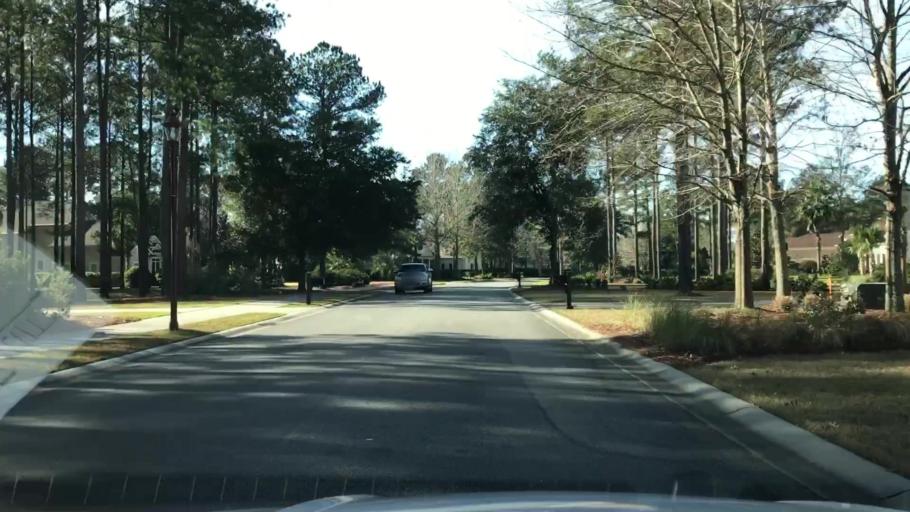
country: US
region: South Carolina
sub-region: Beaufort County
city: Bluffton
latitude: 32.2551
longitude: -80.9082
